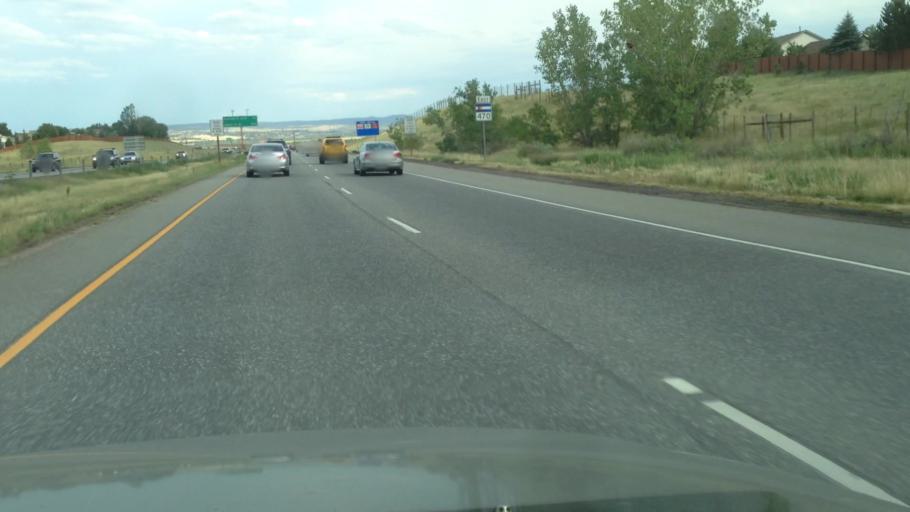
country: US
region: Colorado
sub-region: Jefferson County
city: Ken Caryl
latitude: 39.5577
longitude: -105.0998
